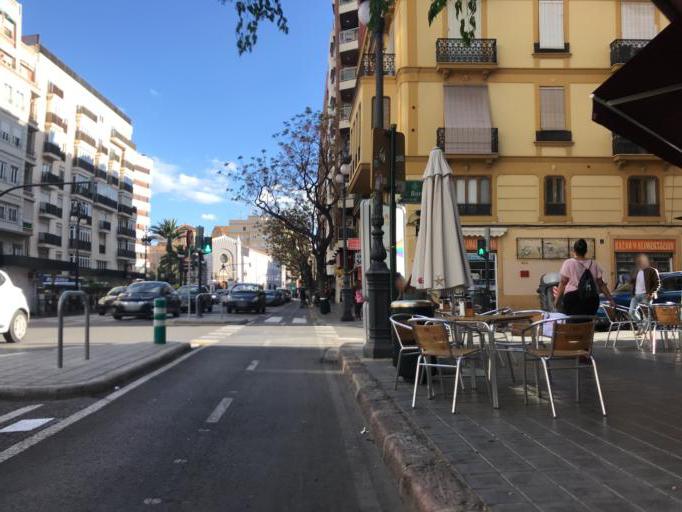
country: ES
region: Valencia
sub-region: Provincia de Valencia
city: Valencia
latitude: 39.4749
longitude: -0.3841
